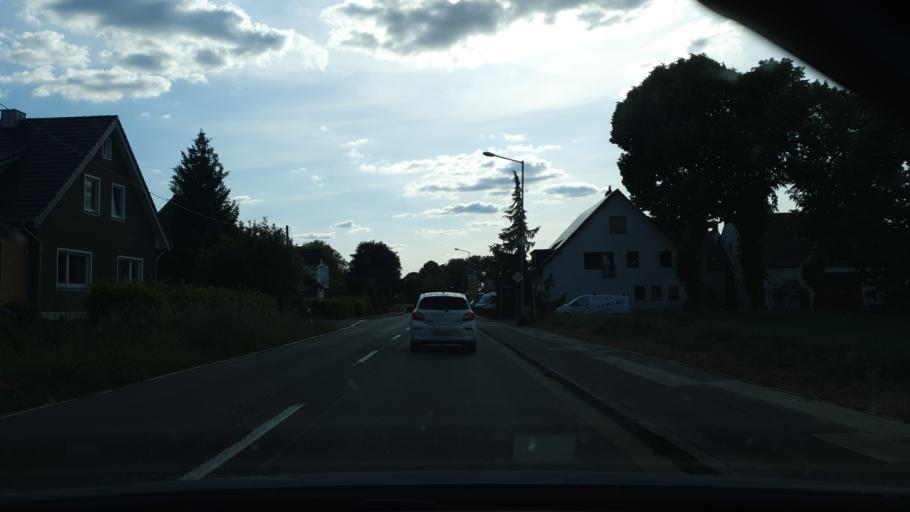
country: DE
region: North Rhine-Westphalia
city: Buende
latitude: 52.1818
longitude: 8.5632
